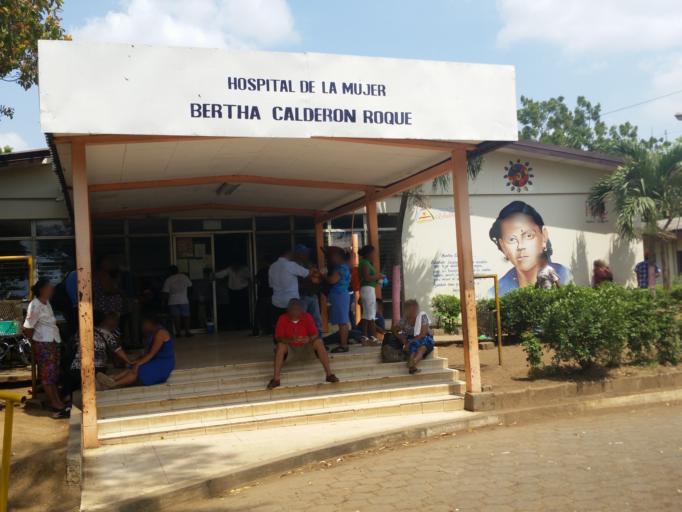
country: NI
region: Managua
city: Managua
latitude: 12.1245
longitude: -86.2984
